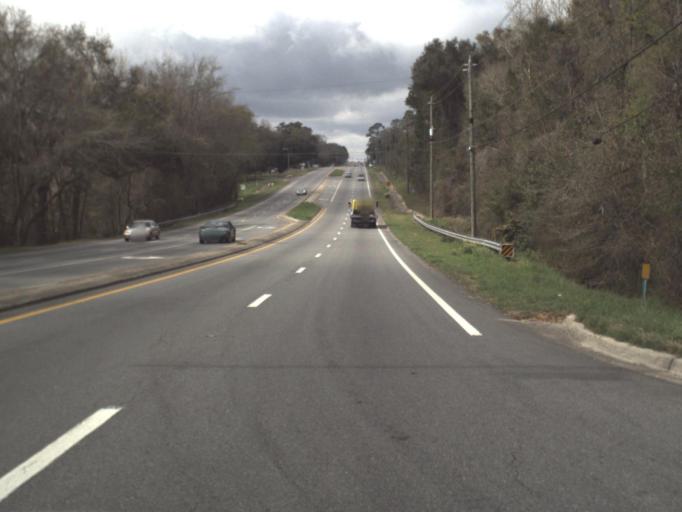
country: US
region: Florida
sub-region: Leon County
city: Tallahassee
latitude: 30.4290
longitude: -84.2027
